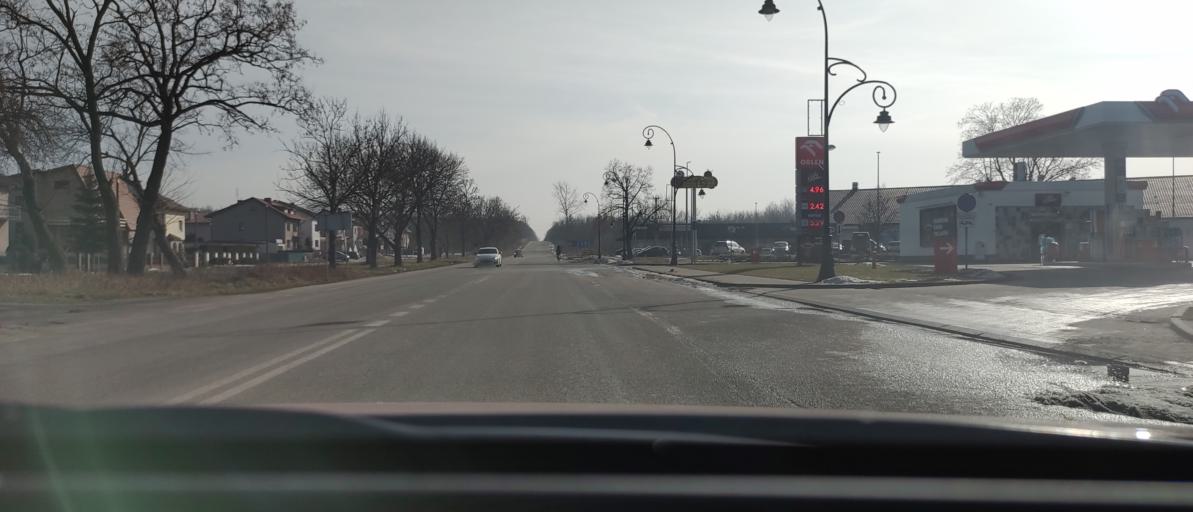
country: PL
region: Masovian Voivodeship
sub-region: Powiat bialobrzeski
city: Bialobrzegi
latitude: 51.6439
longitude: 20.9583
